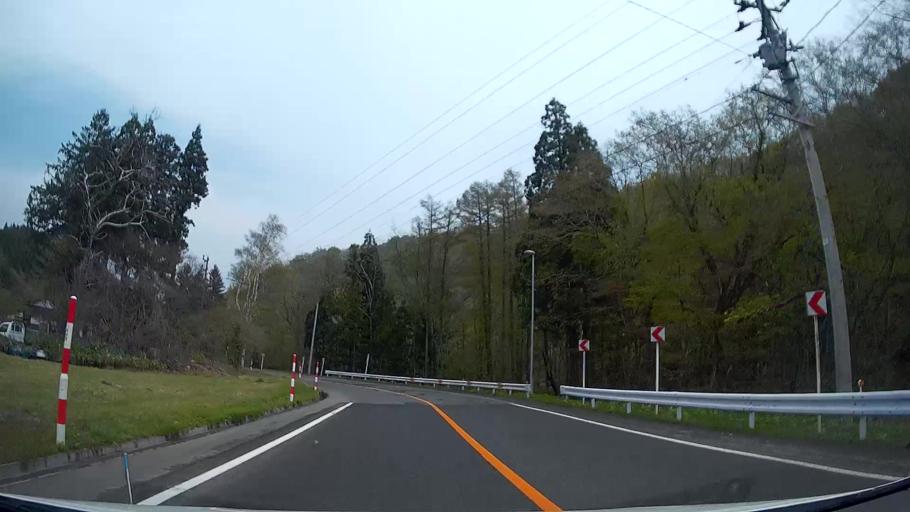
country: JP
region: Akita
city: Hanawa
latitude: 40.3705
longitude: 140.8733
